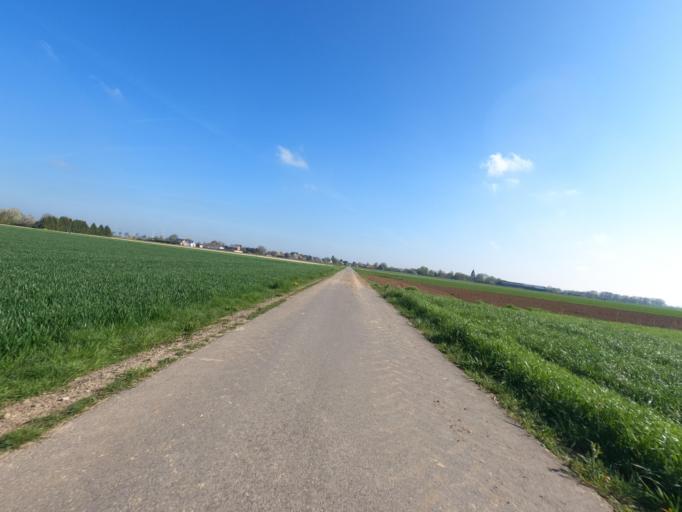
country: DE
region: North Rhine-Westphalia
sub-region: Regierungsbezirk Koln
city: Heinsberg
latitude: 51.0335
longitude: 6.0480
